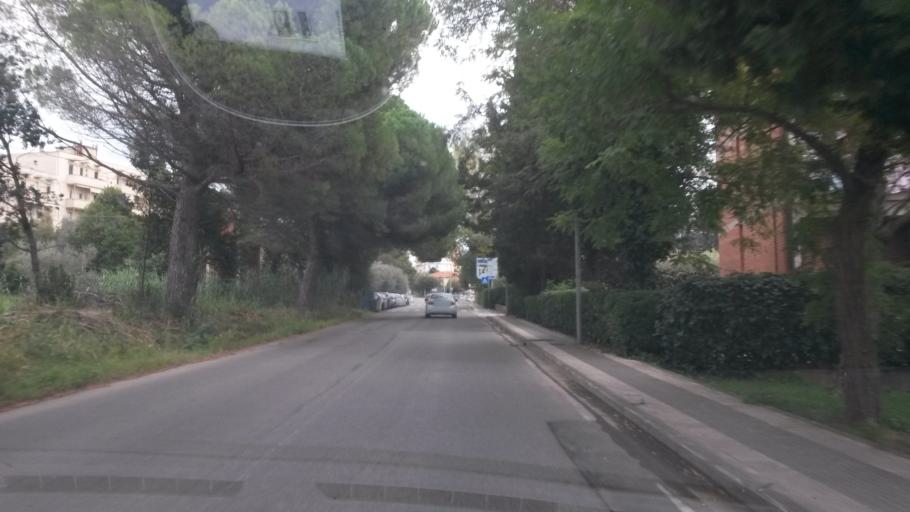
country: IT
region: Tuscany
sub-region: Provincia di Livorno
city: Rosignano Solvay-Castiglioncello
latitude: 43.3992
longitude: 10.4405
